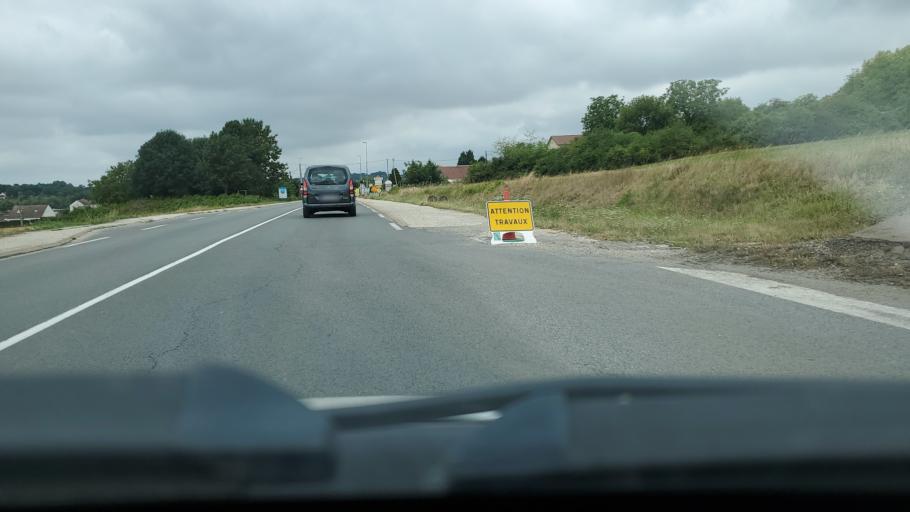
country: FR
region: Ile-de-France
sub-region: Departement de Seine-et-Marne
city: Mouroux
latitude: 48.8169
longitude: 3.0585
